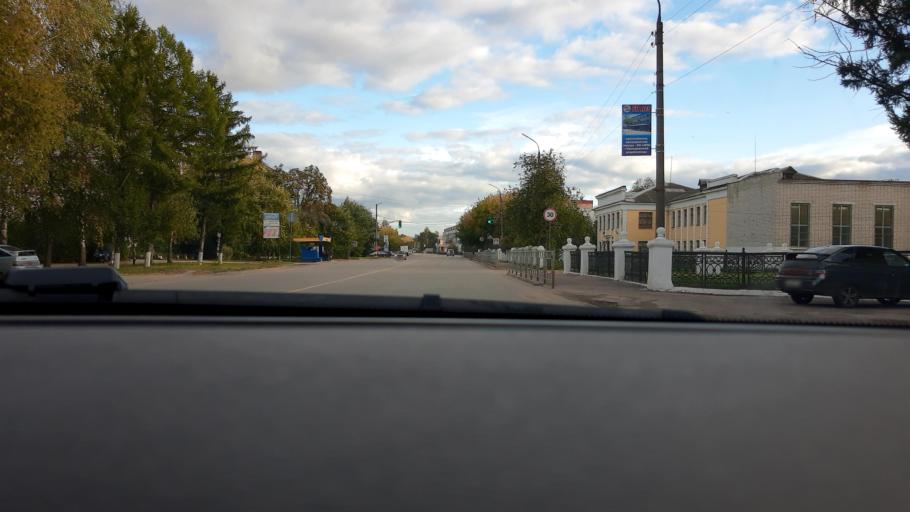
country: RU
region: Nizjnij Novgorod
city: Novaya Balakhna
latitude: 56.5003
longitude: 43.6042
